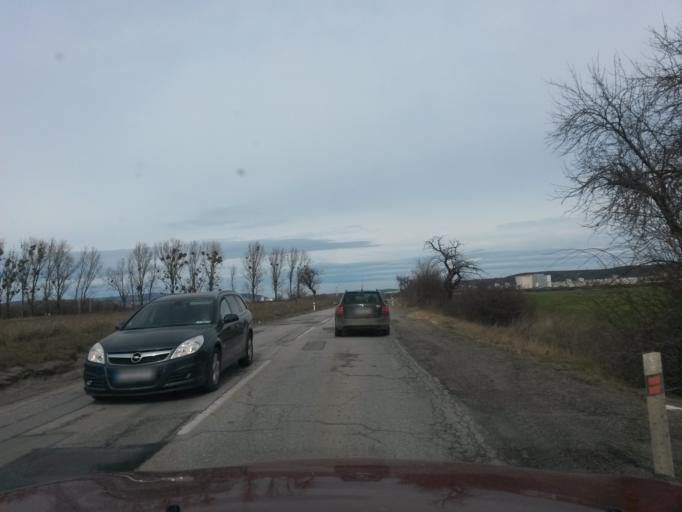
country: SK
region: Kosicky
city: Kosice
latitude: 48.6597
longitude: 21.2767
